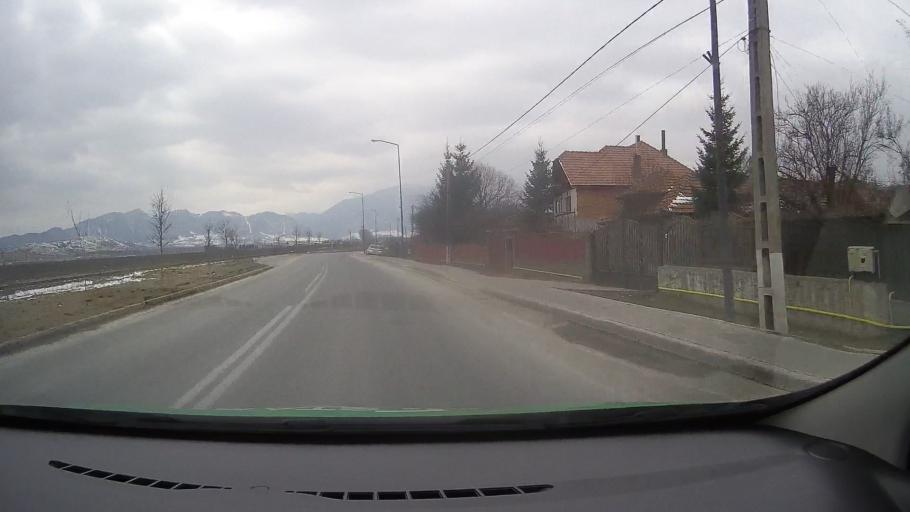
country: RO
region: Brasov
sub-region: Comuna Zarnesti
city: Tohanu Nou
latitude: 45.5773
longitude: 25.3809
